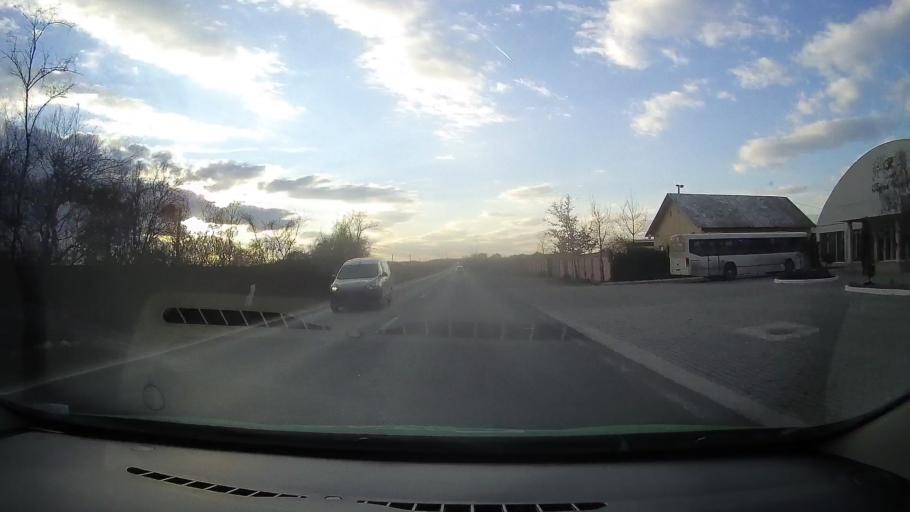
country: RO
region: Dambovita
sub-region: Comuna I. L. Caragiale
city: Mija
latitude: 44.9109
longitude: 25.6871
